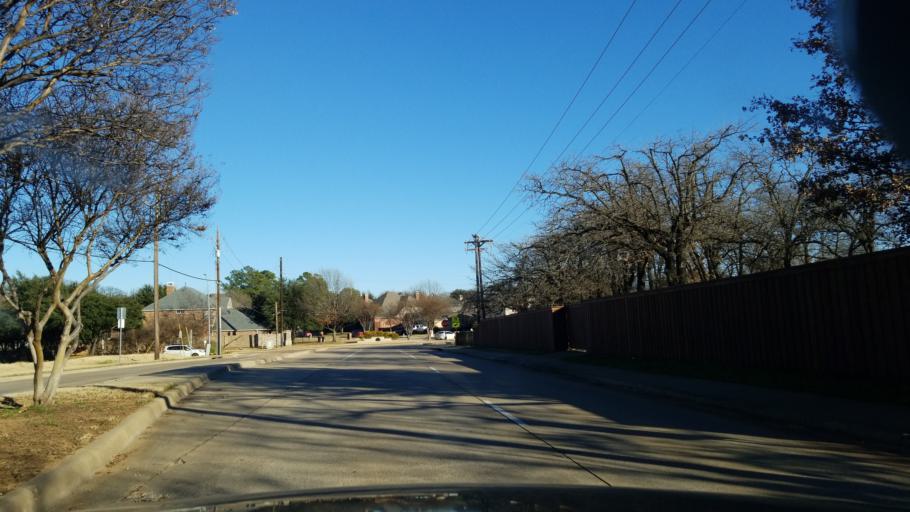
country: US
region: Texas
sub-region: Denton County
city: Corinth
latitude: 33.1551
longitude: -97.0799
